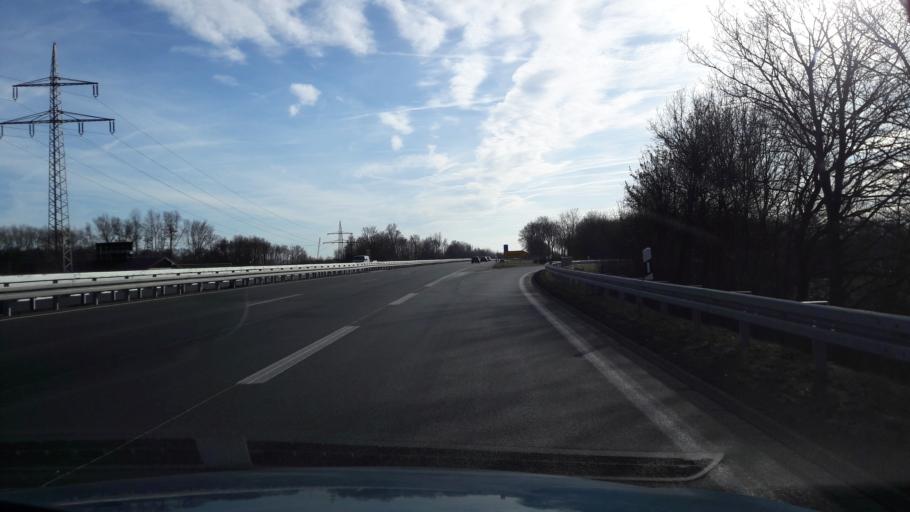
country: DE
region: North Rhine-Westphalia
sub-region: Regierungsbezirk Detmold
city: Rheda-Wiedenbruck
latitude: 51.8375
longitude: 8.3369
